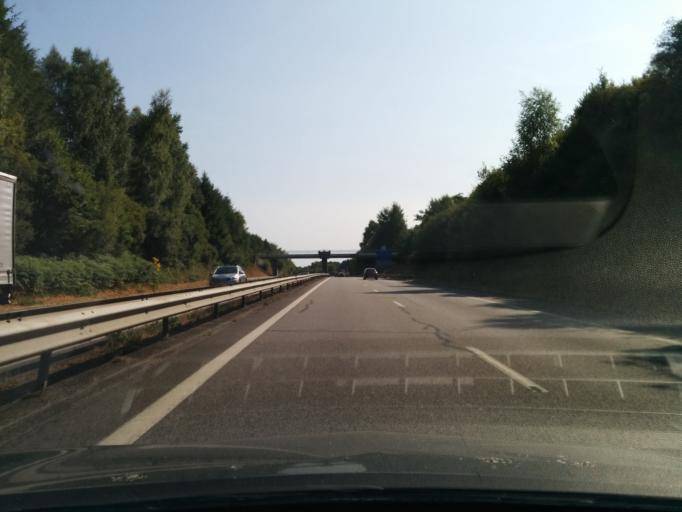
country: FR
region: Limousin
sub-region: Departement de la Haute-Vienne
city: Rilhac-Rancon
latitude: 45.9179
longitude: 1.2965
